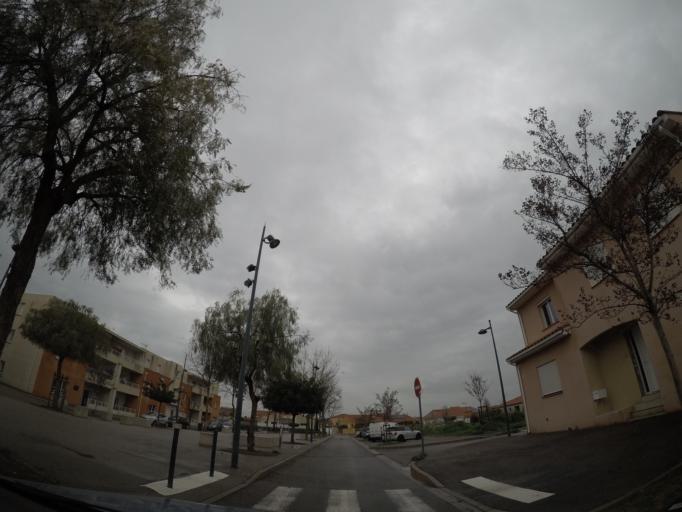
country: FR
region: Languedoc-Roussillon
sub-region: Departement des Pyrenees-Orientales
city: Elne
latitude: 42.6113
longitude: 2.9717
